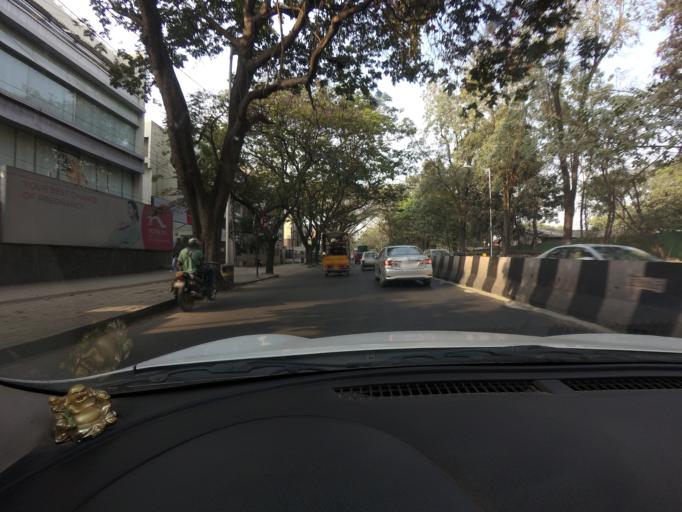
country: IN
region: Karnataka
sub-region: Bangalore Urban
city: Bangalore
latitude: 13.0068
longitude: 77.5839
